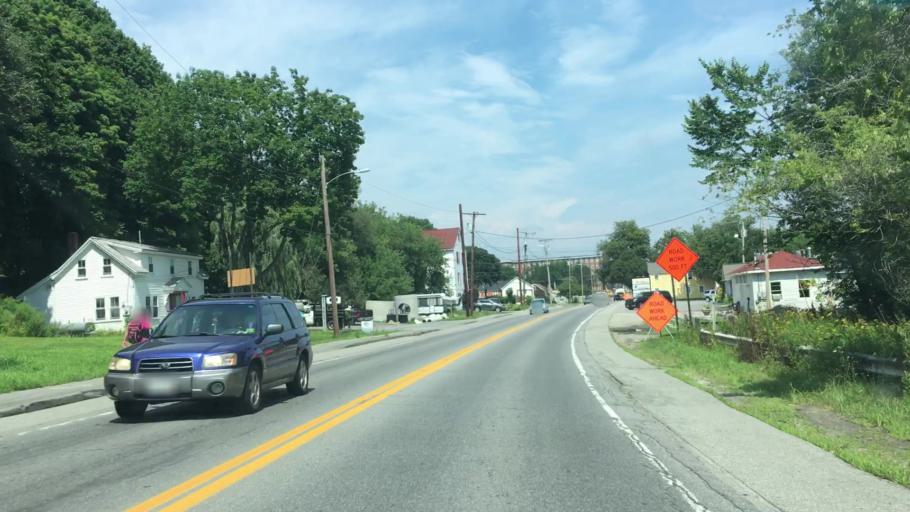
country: US
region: Maine
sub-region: Kennebec County
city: Hallowell
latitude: 44.2808
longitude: -69.7924
